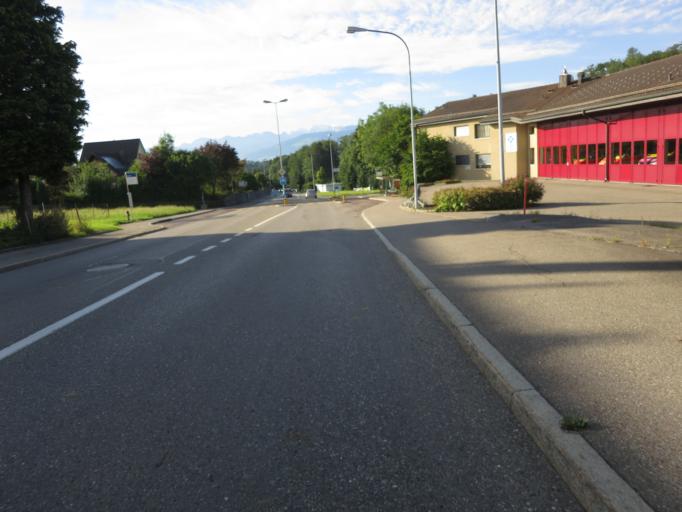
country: CH
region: Zurich
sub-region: Bezirk Meilen
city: Hombrechtikon
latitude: 47.2496
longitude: 8.7680
